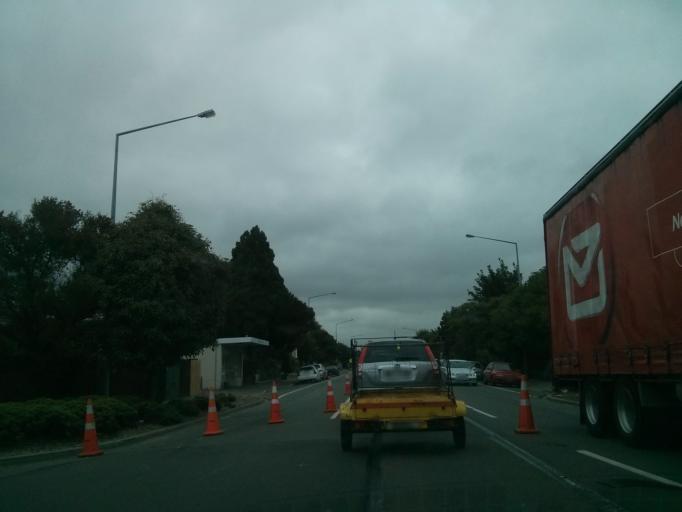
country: NZ
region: Canterbury
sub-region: Christchurch City
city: Christchurch
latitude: -43.5378
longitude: 172.5682
